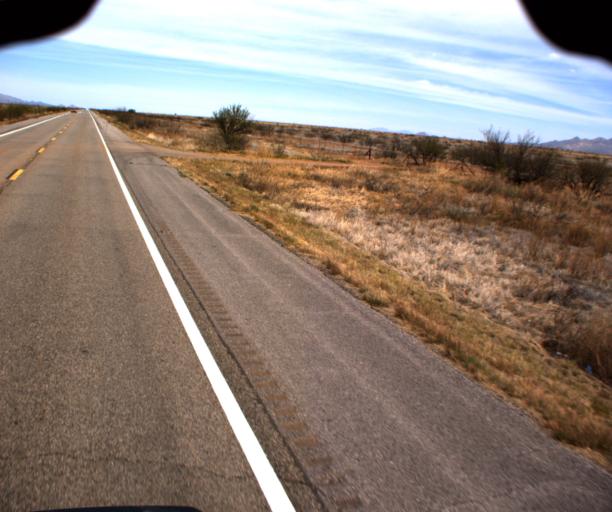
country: US
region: Arizona
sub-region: Cochise County
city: Pirtleville
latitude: 31.5072
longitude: -109.6388
